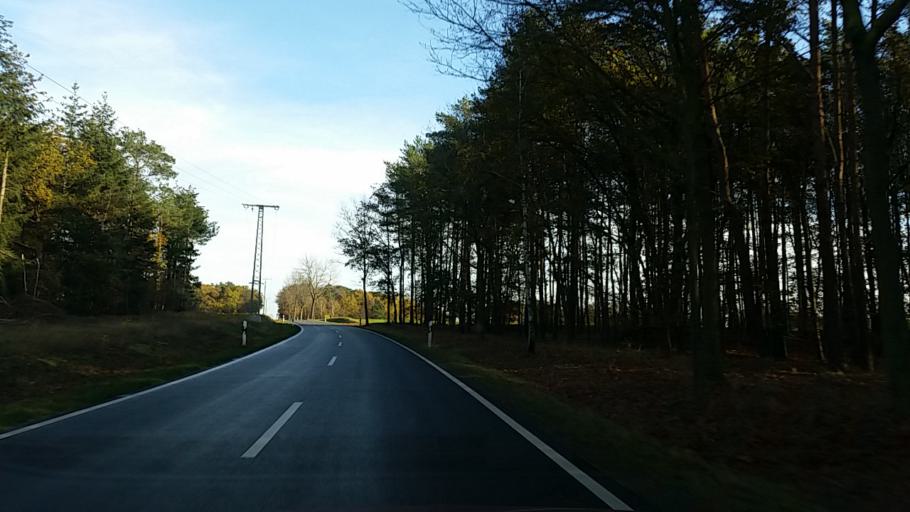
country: DE
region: Lower Saxony
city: Dedelstorf
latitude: 52.6758
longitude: 10.5502
